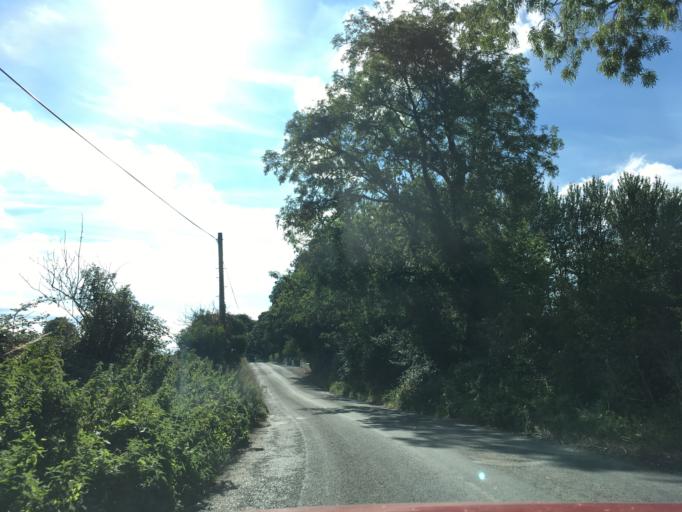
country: IE
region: Munster
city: Cashel
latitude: 52.4581
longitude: -7.9334
